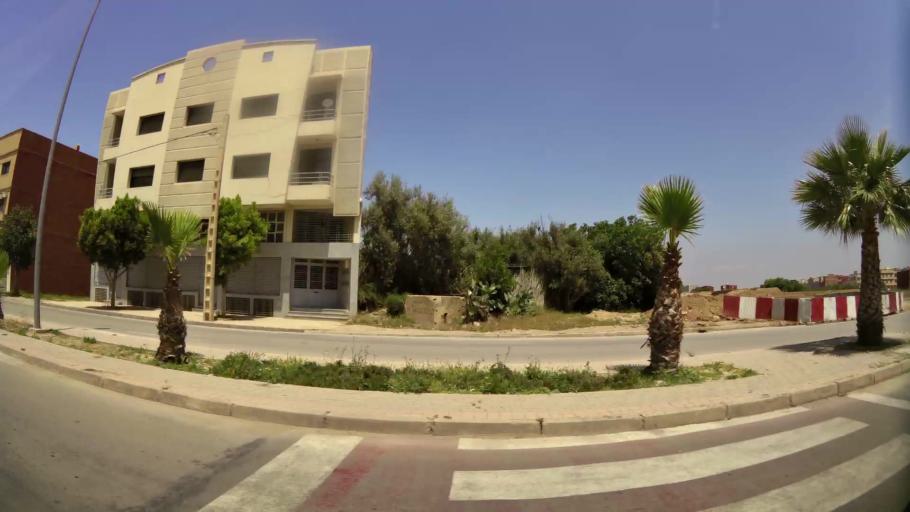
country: MA
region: Oriental
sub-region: Oujda-Angad
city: Oujda
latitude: 34.6923
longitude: -1.8967
